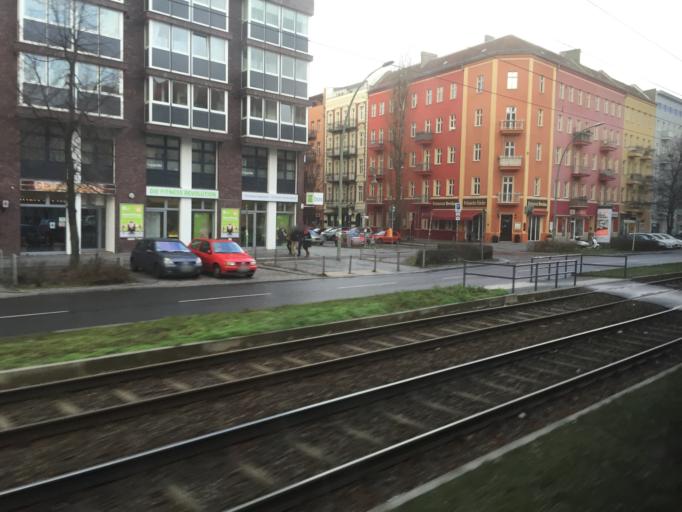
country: DE
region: Berlin
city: Prenzlauer Berg Bezirk
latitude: 52.5369
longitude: 13.4229
